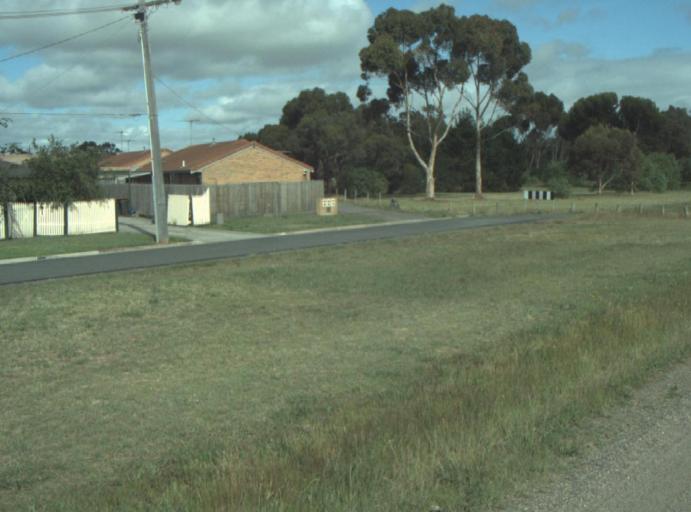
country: AU
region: Victoria
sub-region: Greater Geelong
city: Lara
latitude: -38.0143
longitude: 144.3882
